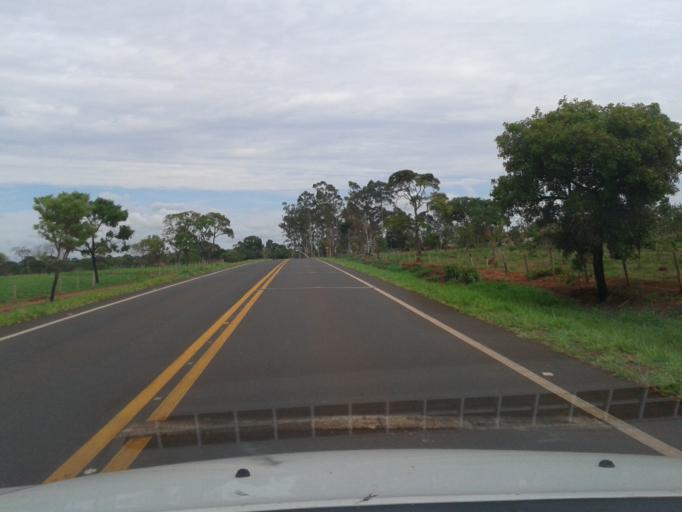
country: BR
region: Minas Gerais
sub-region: Iturama
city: Iturama
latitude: -19.5646
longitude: -50.0178
